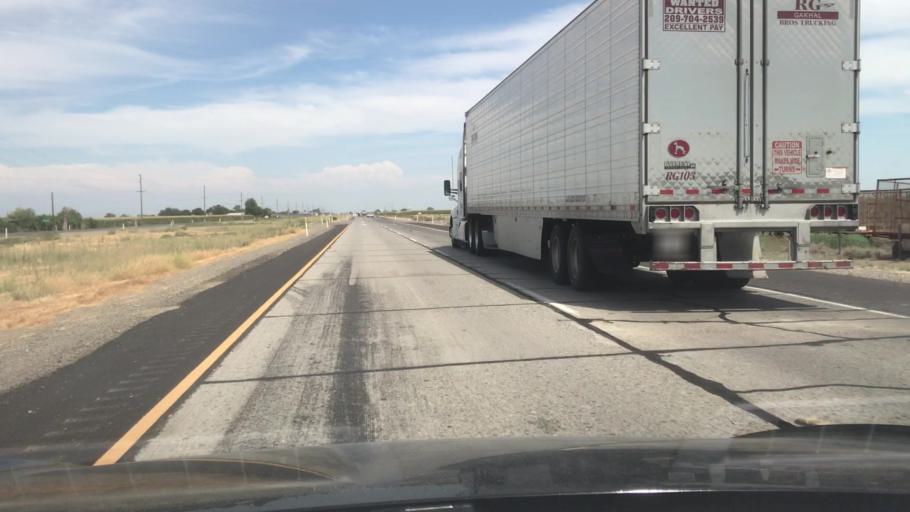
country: US
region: California
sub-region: Merced County
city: South Dos Palos
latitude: 37.0544
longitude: -120.7189
